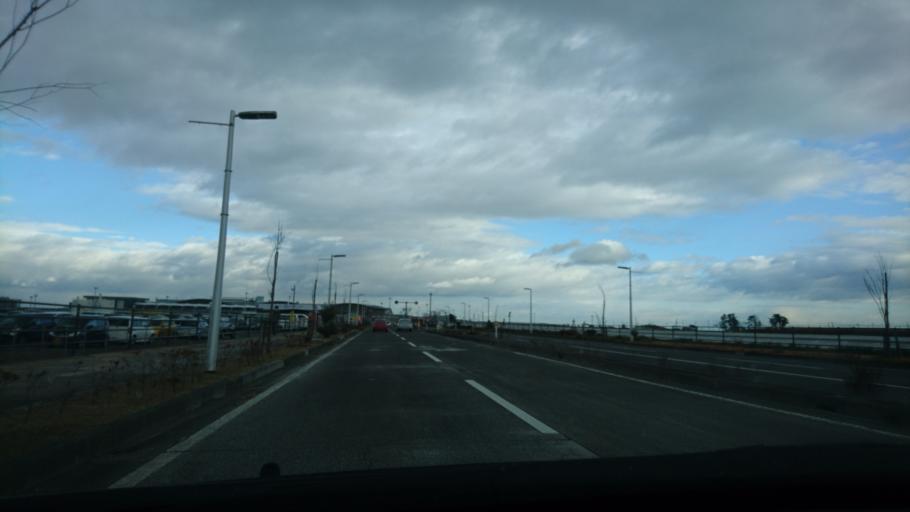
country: JP
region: Miyagi
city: Iwanuma
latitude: 38.1323
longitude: 140.9304
